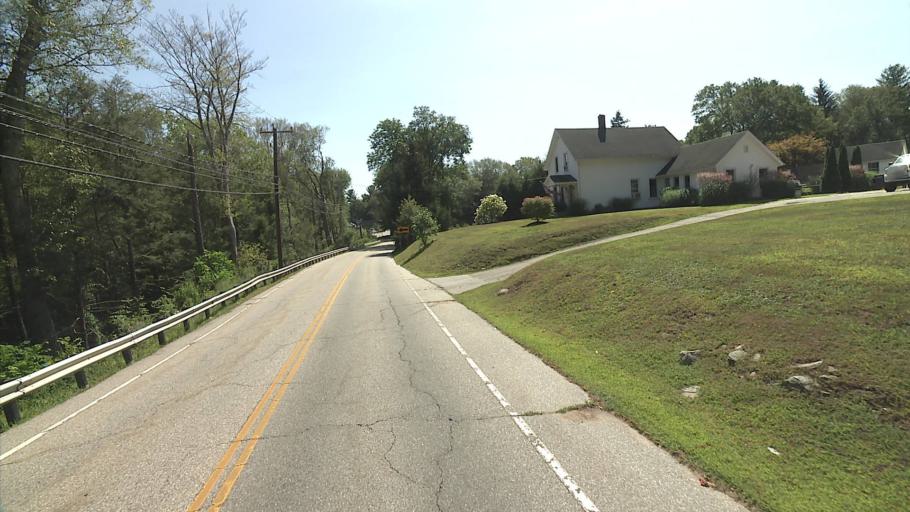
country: US
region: Connecticut
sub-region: New London County
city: Jewett City
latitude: 41.6009
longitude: -71.9916
